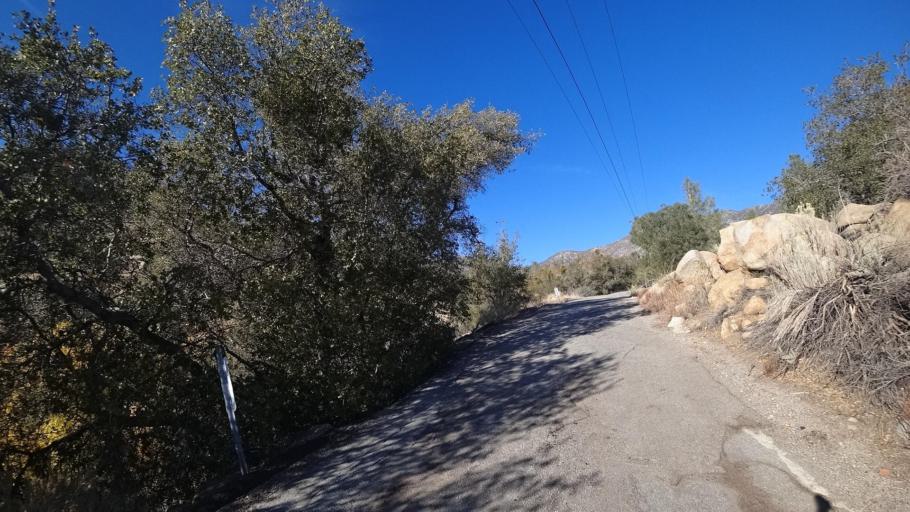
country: US
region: California
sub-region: Kern County
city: Weldon
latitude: 35.7214
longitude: -118.3065
